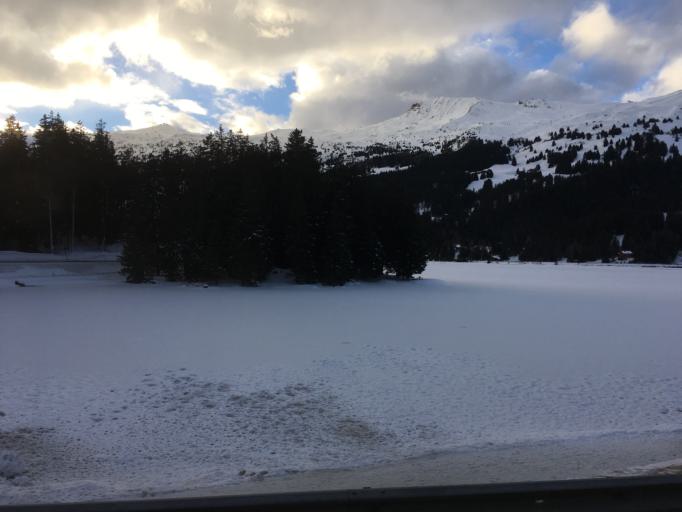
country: CH
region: Grisons
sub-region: Plessur District
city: Churwalden
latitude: 46.7402
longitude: 9.5559
